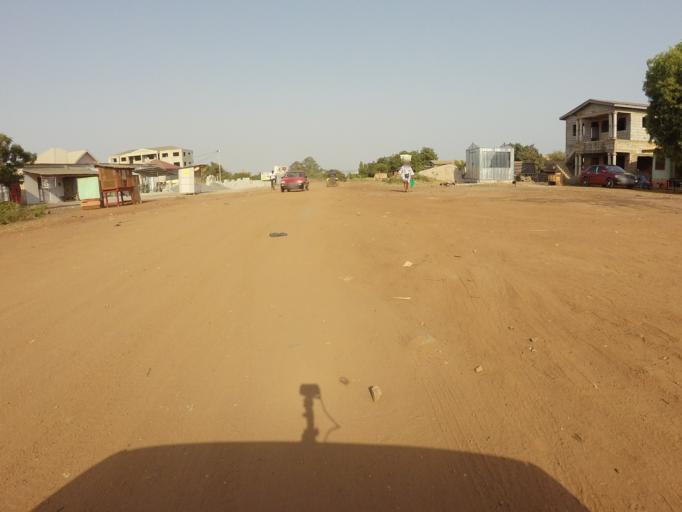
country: GH
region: Greater Accra
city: Tema
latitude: 5.7005
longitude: 0.0590
